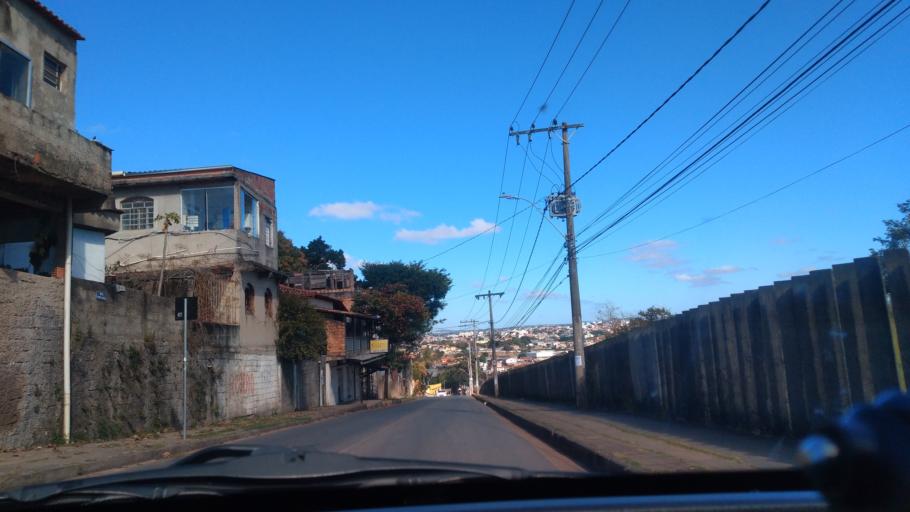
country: BR
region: Minas Gerais
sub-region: Santa Luzia
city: Santa Luzia
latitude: -19.8096
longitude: -43.9401
